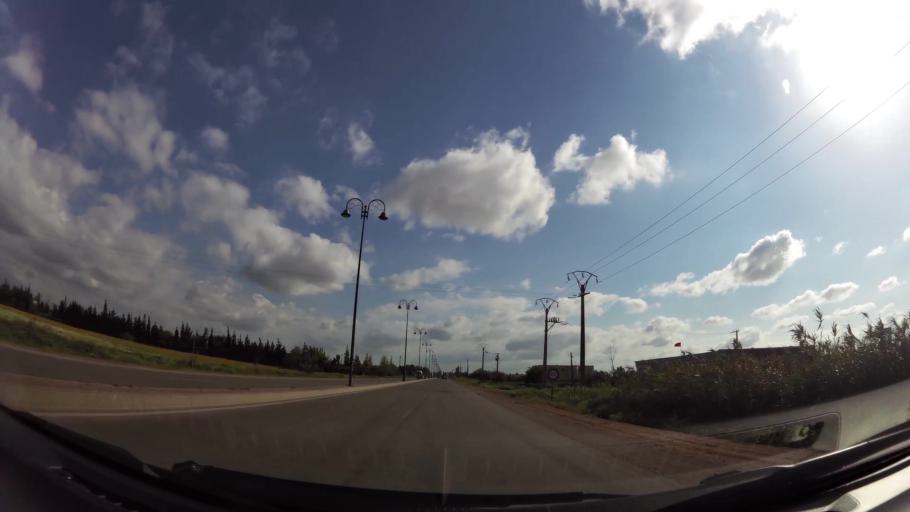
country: MA
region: Chaouia-Ouardigha
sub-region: Settat Province
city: Berrechid
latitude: 33.2948
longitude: -7.5747
